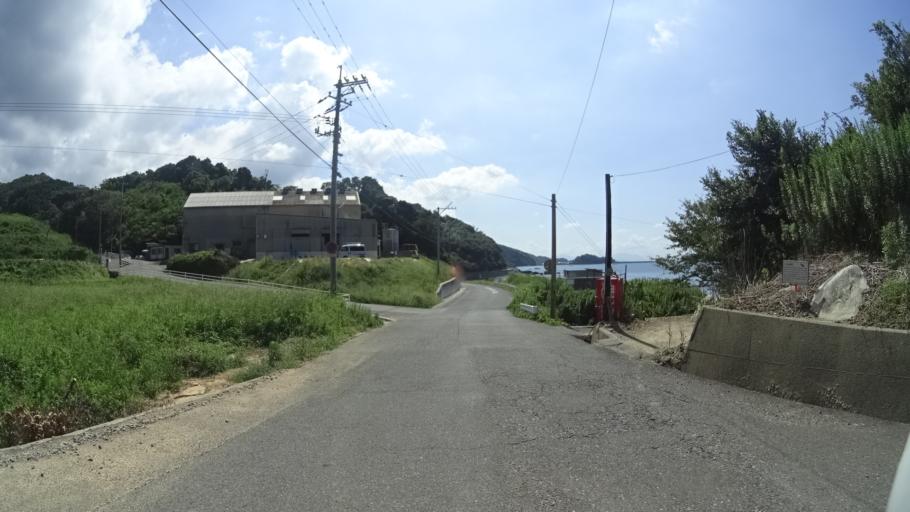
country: JP
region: Yamaguchi
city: Shimonoseki
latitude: 34.1028
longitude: 130.8688
